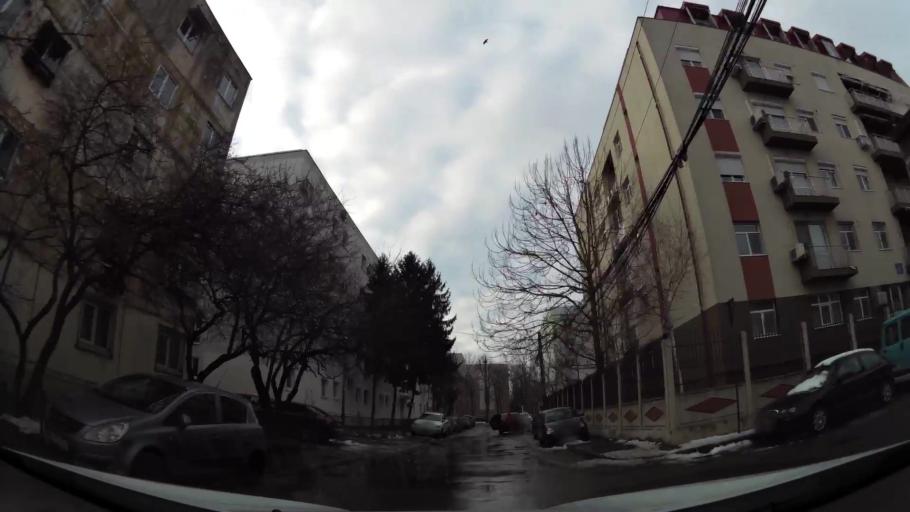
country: RO
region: Ilfov
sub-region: Comuna Popesti-Leordeni
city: Popesti-Leordeni
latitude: 44.4074
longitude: 26.1779
